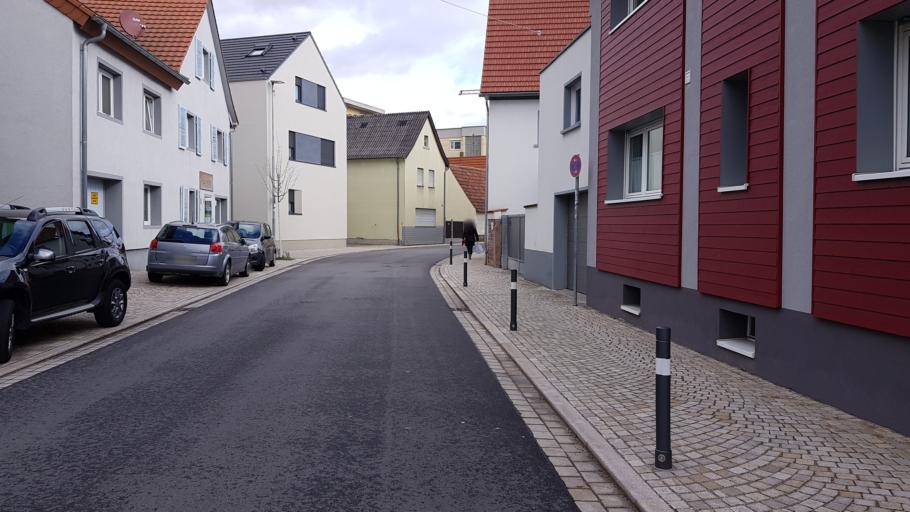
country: DE
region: Baden-Wuerttemberg
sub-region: Karlsruhe Region
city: Sandhausen
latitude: 49.3350
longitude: 8.6694
